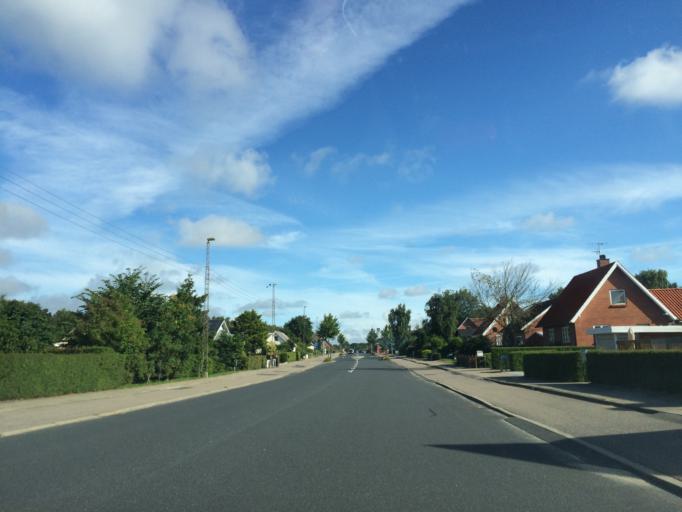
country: DK
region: Central Jutland
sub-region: Viborg Kommune
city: Viborg
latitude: 56.4261
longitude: 9.4033
